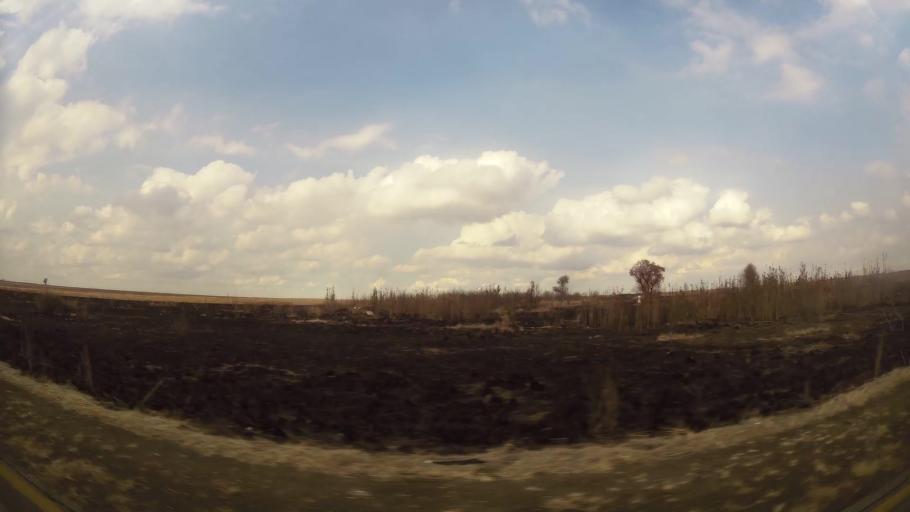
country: ZA
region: Orange Free State
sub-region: Fezile Dabi District Municipality
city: Sasolburg
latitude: -26.8411
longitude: 27.8928
